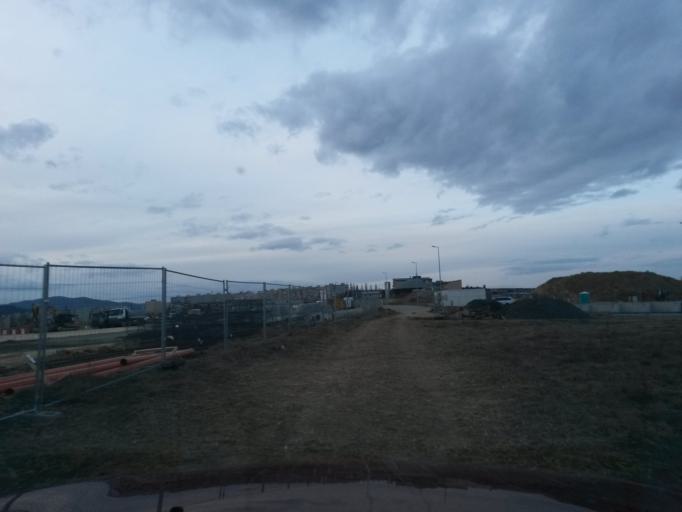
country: SK
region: Kosicky
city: Kosice
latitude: 48.7260
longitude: 21.2946
